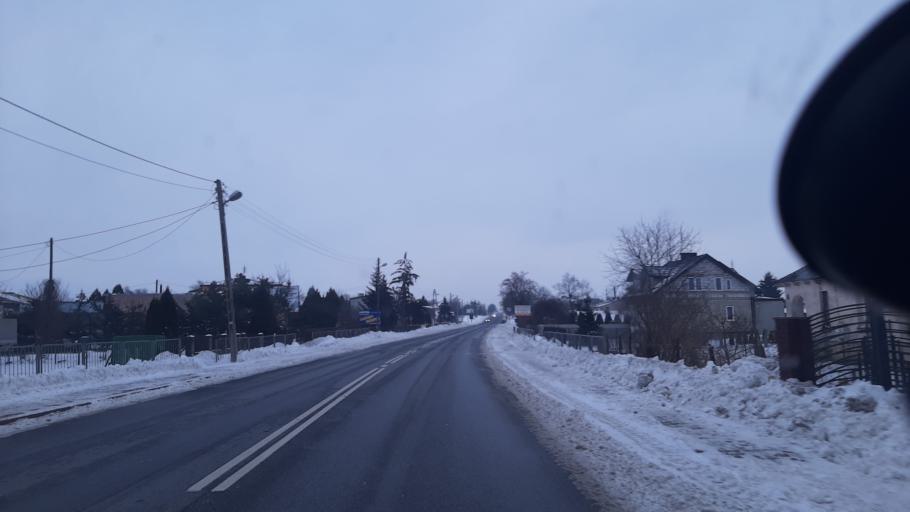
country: PL
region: Lublin Voivodeship
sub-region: Powiat pulawski
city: Markuszow
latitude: 51.3738
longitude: 22.2653
